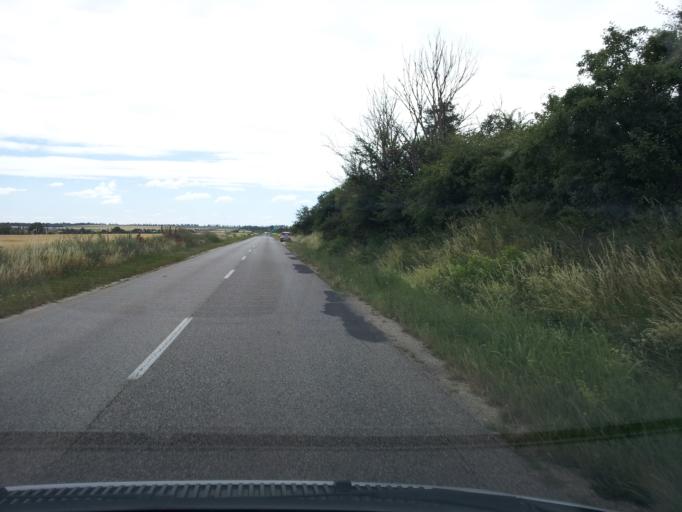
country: HU
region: Veszprem
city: Liter
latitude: 47.0861
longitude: 18.0531
